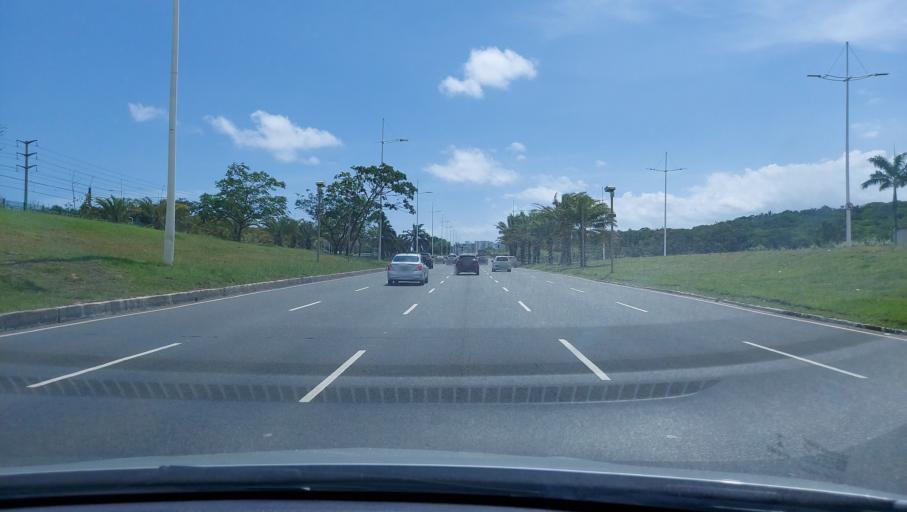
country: BR
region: Bahia
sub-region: Lauro De Freitas
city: Lauro de Freitas
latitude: -12.9284
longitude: -38.3876
